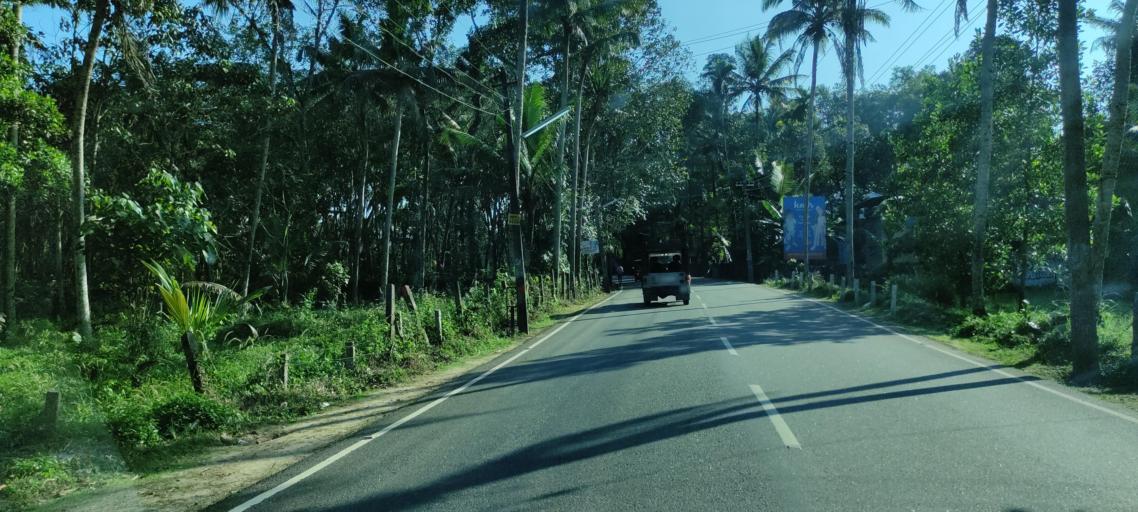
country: IN
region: Kerala
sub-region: Pattanamtitta
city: Adur
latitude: 9.1888
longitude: 76.7448
